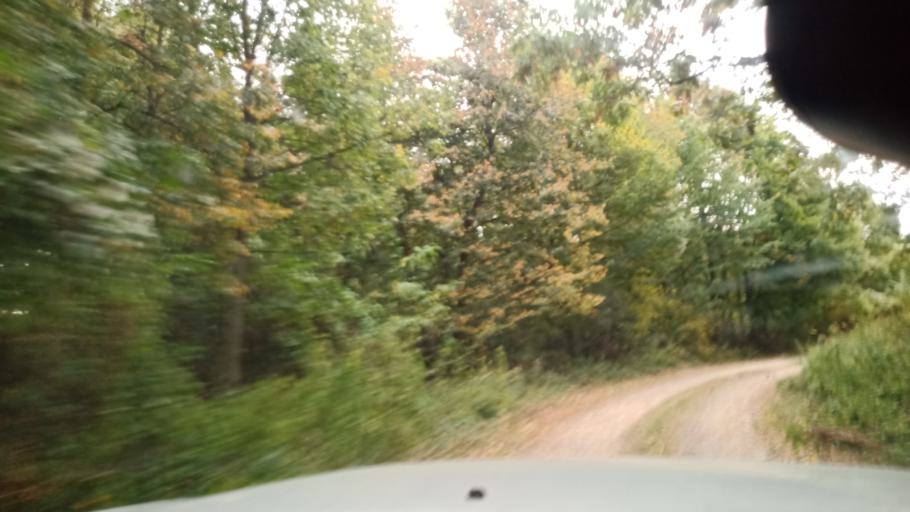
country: HU
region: Fejer
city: Mor
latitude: 47.3860
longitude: 18.2497
